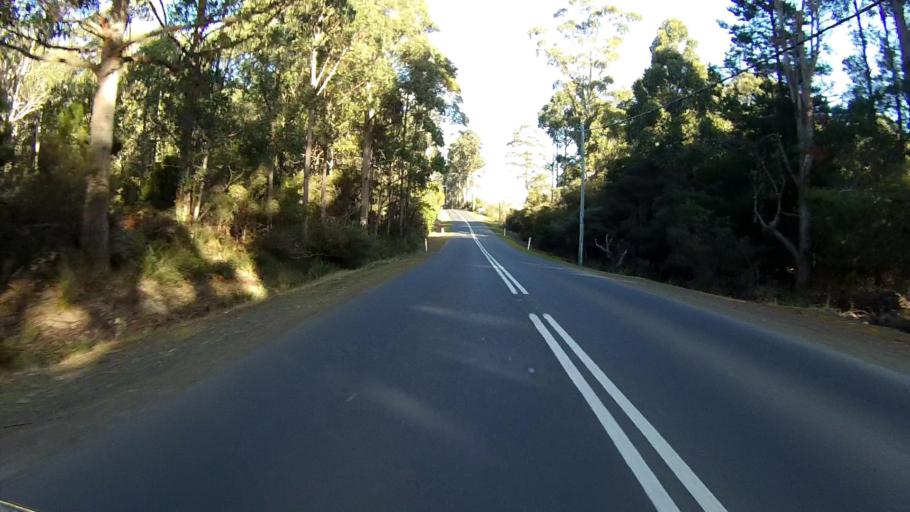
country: AU
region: Tasmania
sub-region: Clarence
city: Sandford
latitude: -43.1309
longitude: 147.8496
